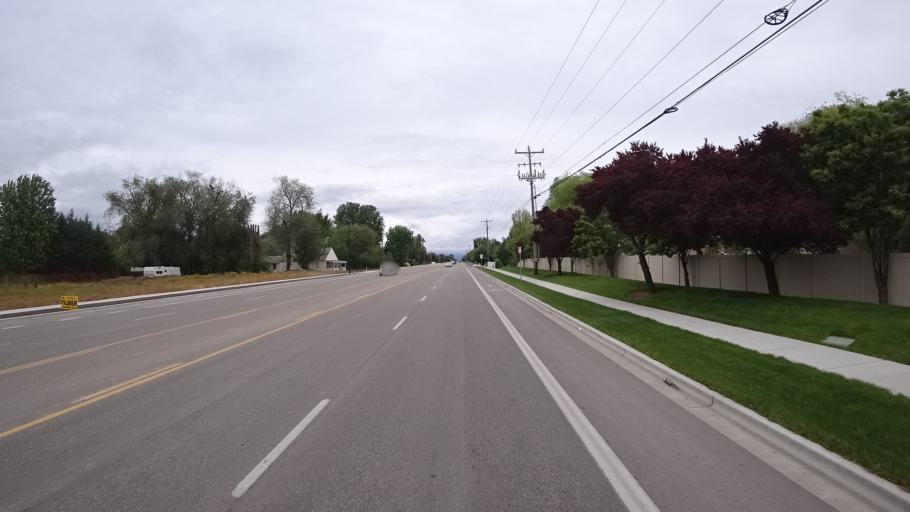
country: US
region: Idaho
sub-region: Ada County
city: Meridian
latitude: 43.6337
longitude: -116.3854
